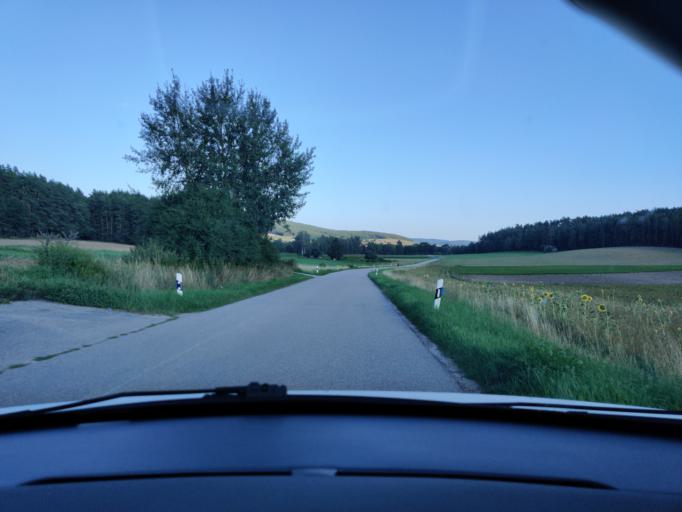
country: DE
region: Bavaria
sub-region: Upper Palatinate
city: Stulln
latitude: 49.4194
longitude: 12.1523
